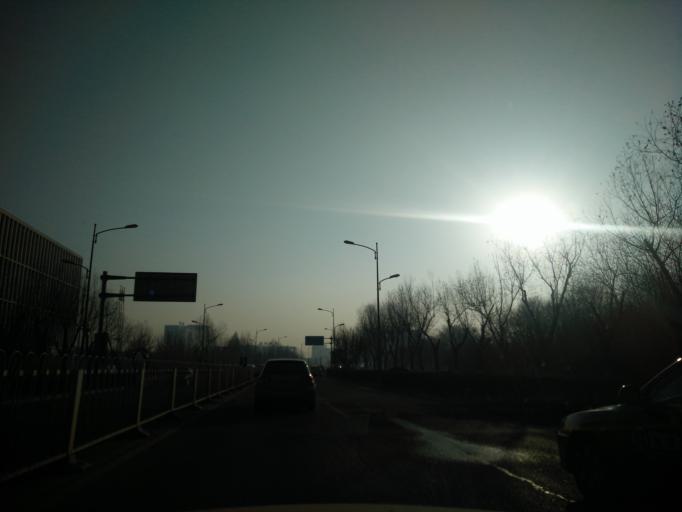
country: CN
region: Beijing
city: Jiugong
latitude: 39.7742
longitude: 116.5078
